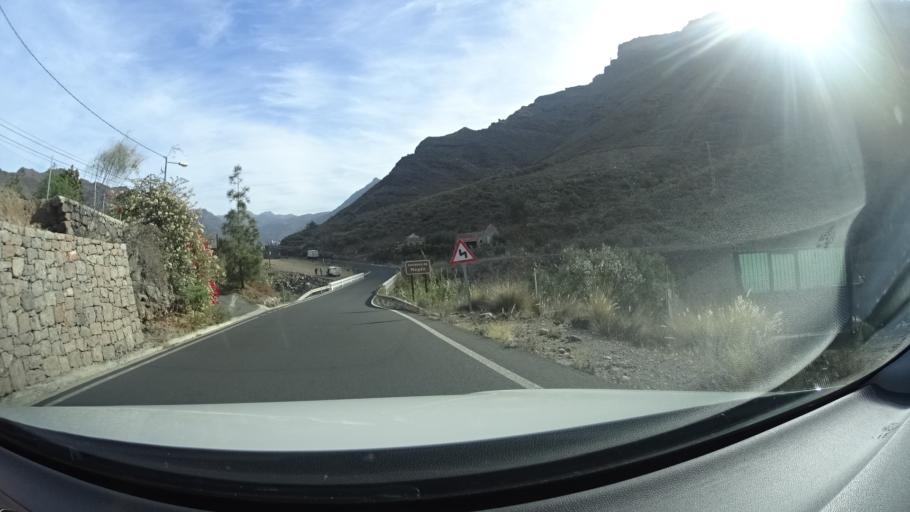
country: ES
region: Canary Islands
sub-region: Provincia de Las Palmas
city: Mogan
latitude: 27.8649
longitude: -15.7410
